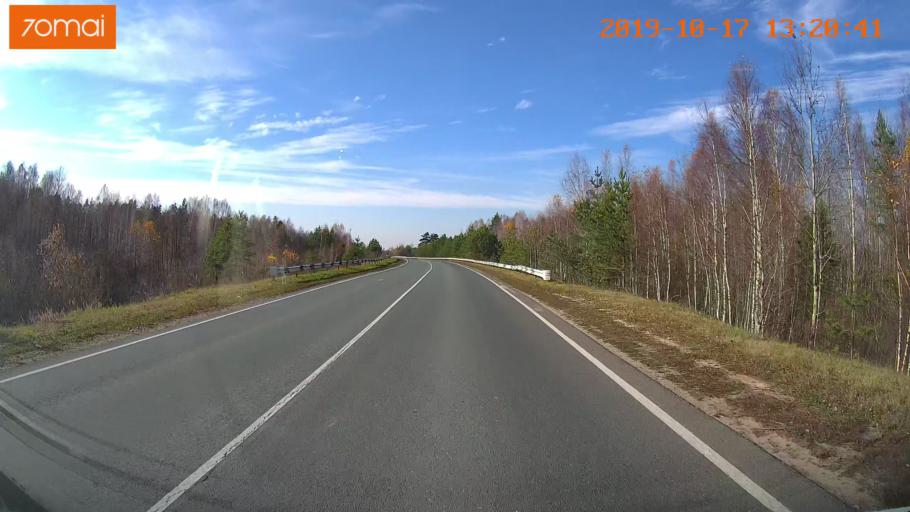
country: RU
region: Rjazan
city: Gus'-Zheleznyy
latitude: 55.0779
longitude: 41.0455
